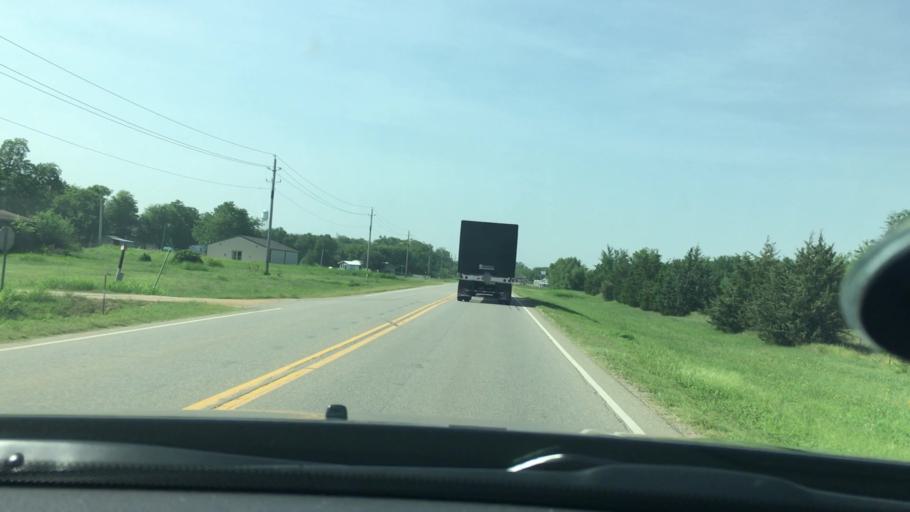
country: US
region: Oklahoma
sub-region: Coal County
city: Coalgate
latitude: 34.4762
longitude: -96.2180
